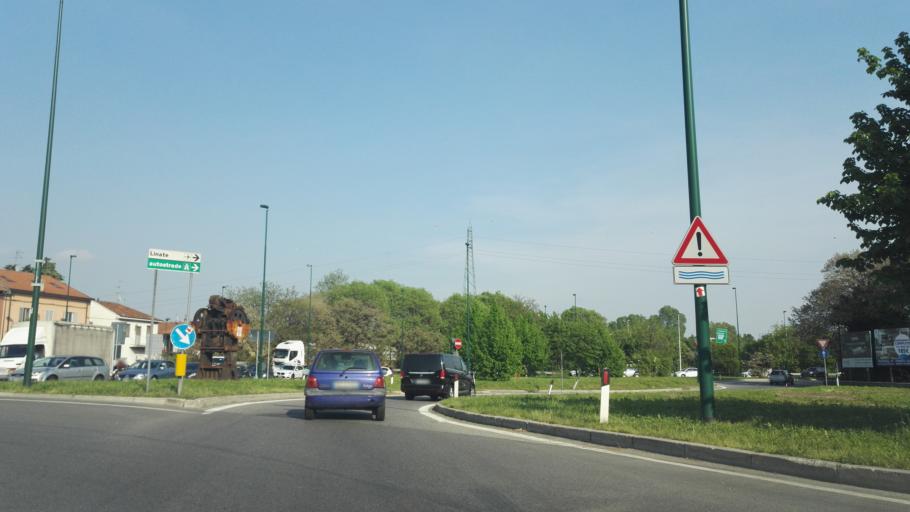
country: IT
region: Lombardy
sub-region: Citta metropolitana di Milano
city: Sesto San Giovanni
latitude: 45.5477
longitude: 9.2564
